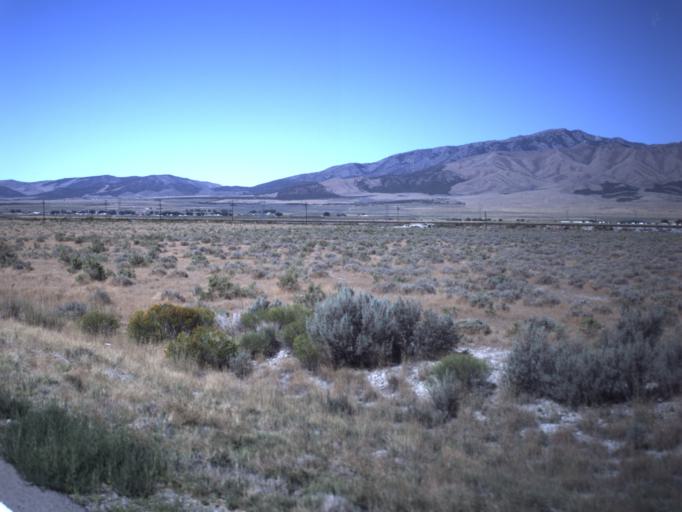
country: US
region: Utah
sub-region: Tooele County
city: Tooele
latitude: 40.3687
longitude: -112.4044
